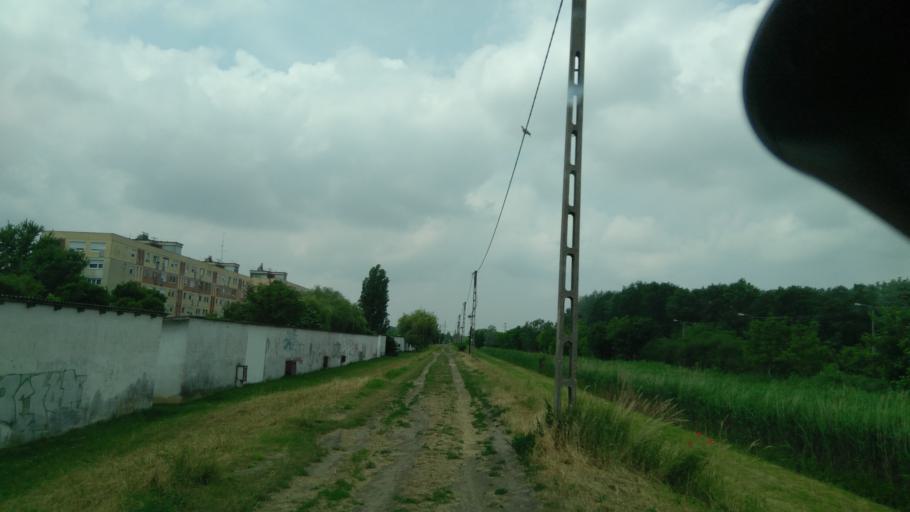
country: HU
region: Bekes
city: Gyula
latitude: 46.6566
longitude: 21.2623
